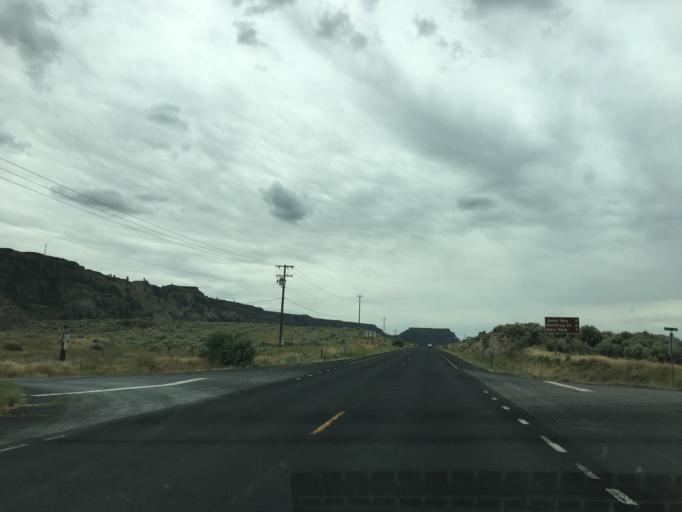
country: US
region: Washington
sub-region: Okanogan County
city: Coulee Dam
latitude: 47.9180
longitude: -119.0543
